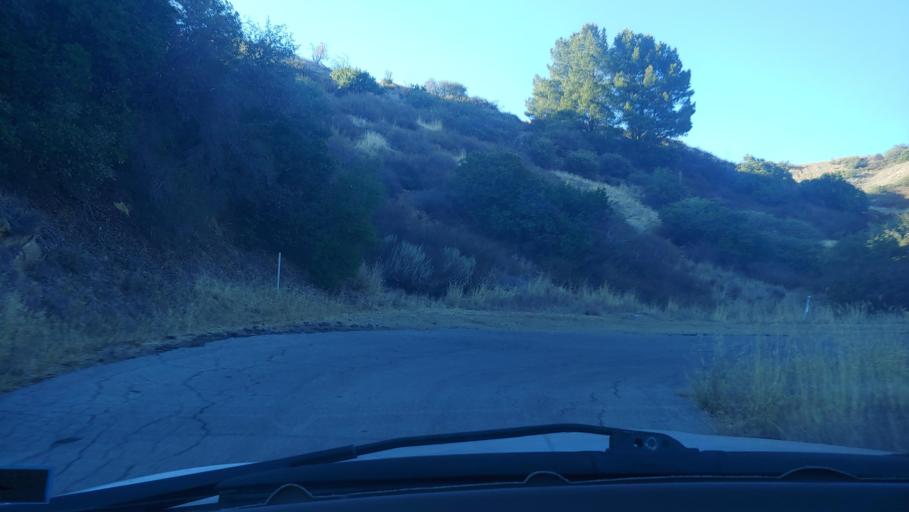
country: US
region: California
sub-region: Santa Barbara County
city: Goleta
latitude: 34.5159
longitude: -119.7960
